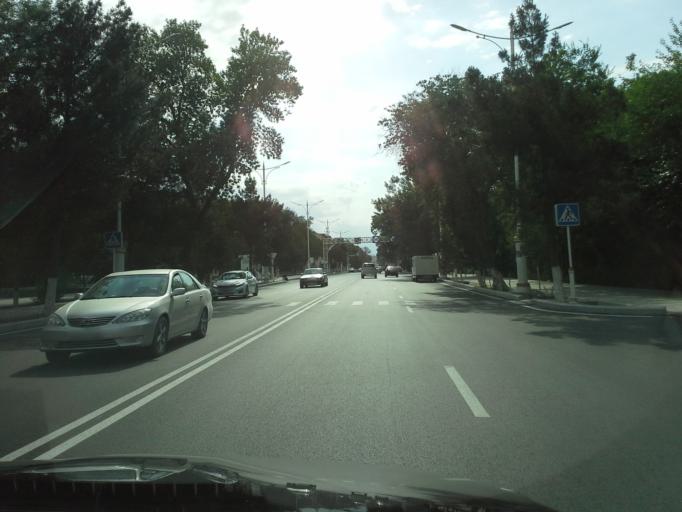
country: TM
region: Ahal
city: Ashgabat
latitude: 37.9579
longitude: 58.3563
